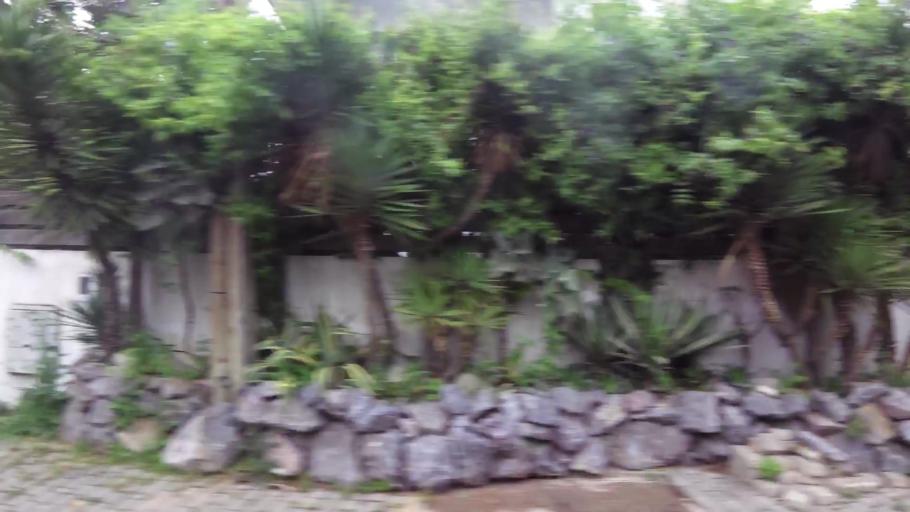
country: MA
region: Grand Casablanca
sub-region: Casablanca
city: Casablanca
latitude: 33.5839
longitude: -7.6554
